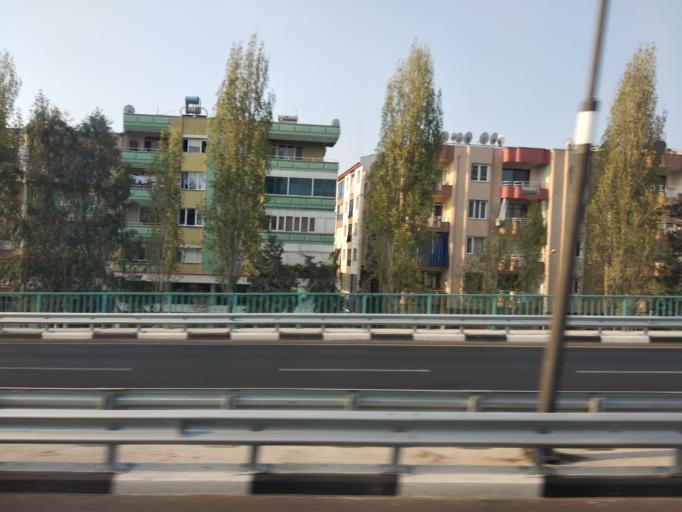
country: TR
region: Manisa
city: Salihli
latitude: 38.4902
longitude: 28.1438
